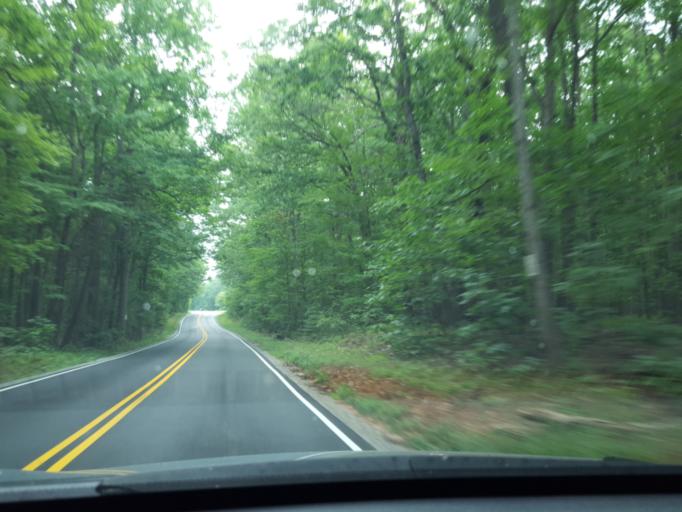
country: US
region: Virginia
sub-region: Spotsylvania County
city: Spotsylvania
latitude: 38.2918
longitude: -77.7220
